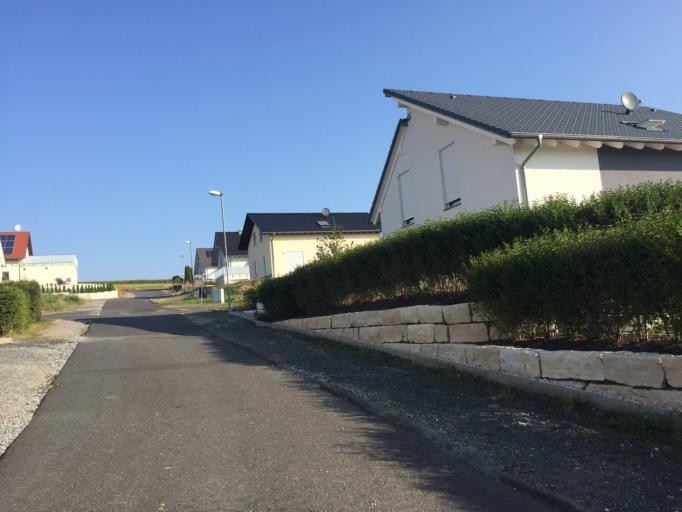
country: DE
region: Hesse
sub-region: Regierungsbezirk Giessen
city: Hoernsheim
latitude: 50.4636
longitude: 8.6010
